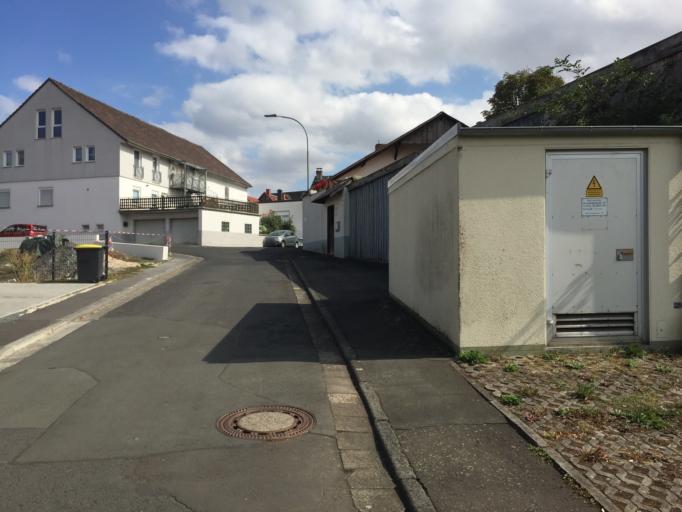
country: DE
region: Hesse
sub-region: Regierungsbezirk Giessen
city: Lich
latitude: 50.4798
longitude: 8.8306
